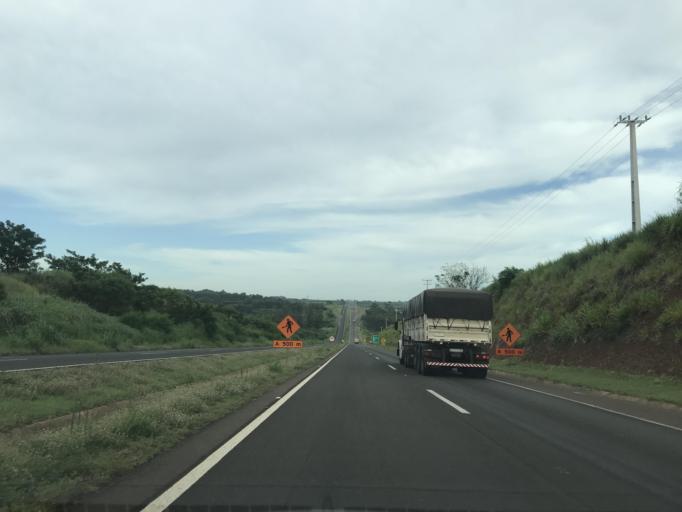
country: BR
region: Parana
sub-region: Alto Parana
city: Alto Parana
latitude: -23.1160
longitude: -52.3251
